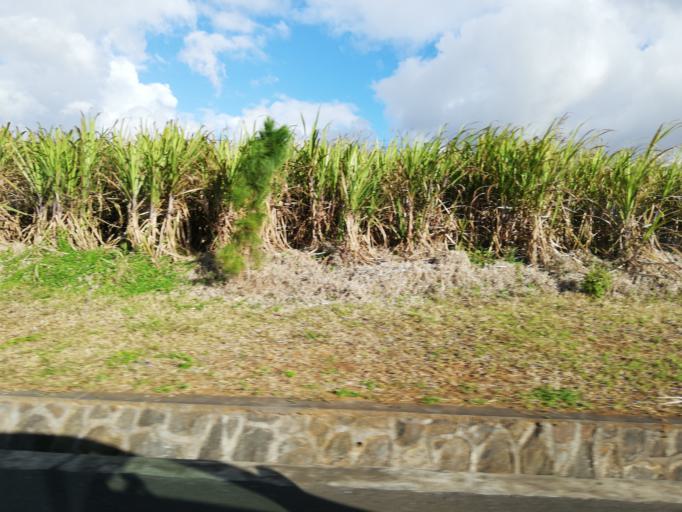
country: MU
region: Moka
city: Quartier Militaire
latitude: -20.2439
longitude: 57.5922
